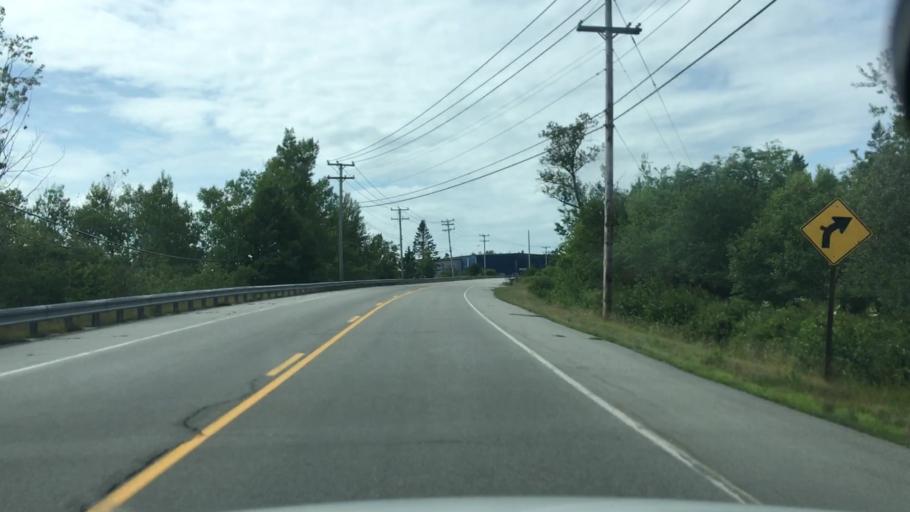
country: US
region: Maine
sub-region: Washington County
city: Eastport
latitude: 44.9264
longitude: -67.0219
